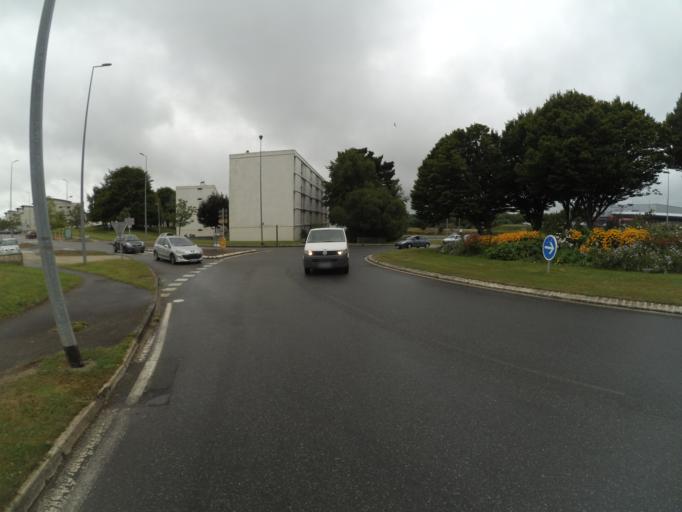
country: FR
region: Brittany
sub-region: Departement du Finistere
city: Morlaix
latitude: 48.5929
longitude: -3.8293
